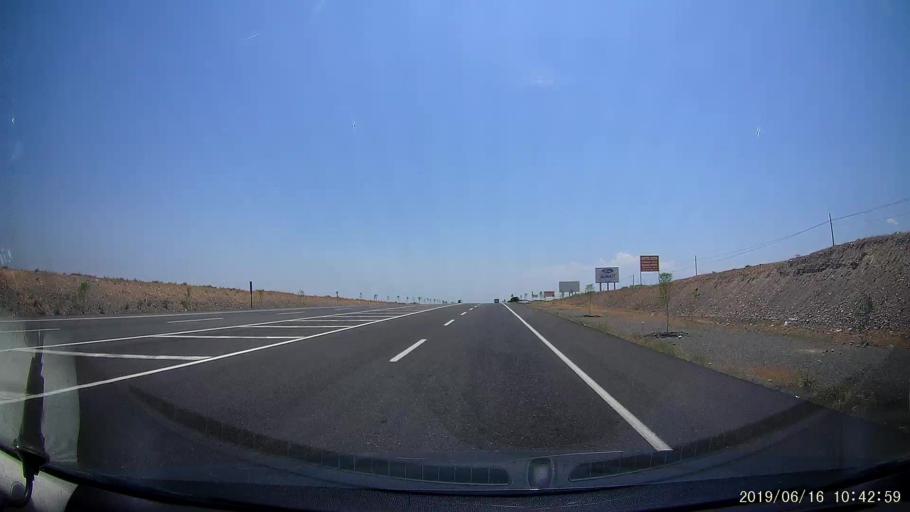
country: AM
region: Armavir
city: Shenavan
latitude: 40.0383
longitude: 43.8185
